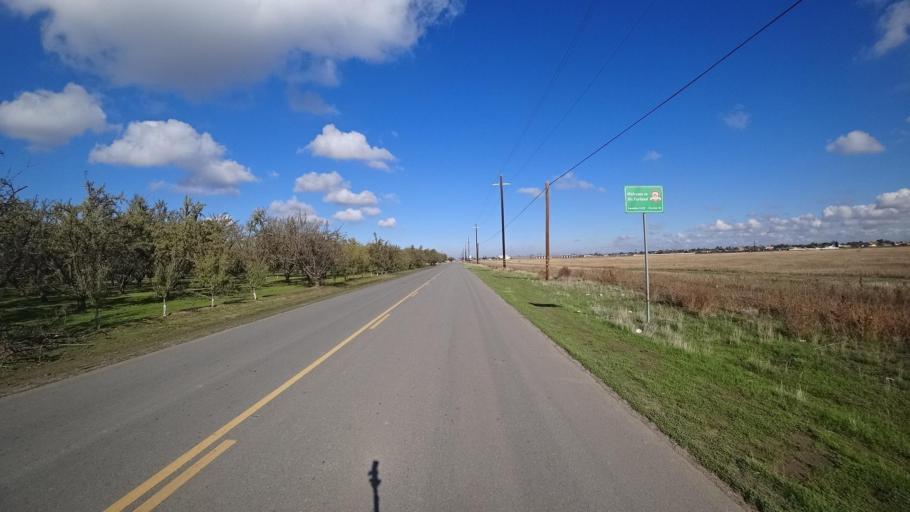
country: US
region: California
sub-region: Kern County
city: McFarland
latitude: 35.6608
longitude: -119.2403
